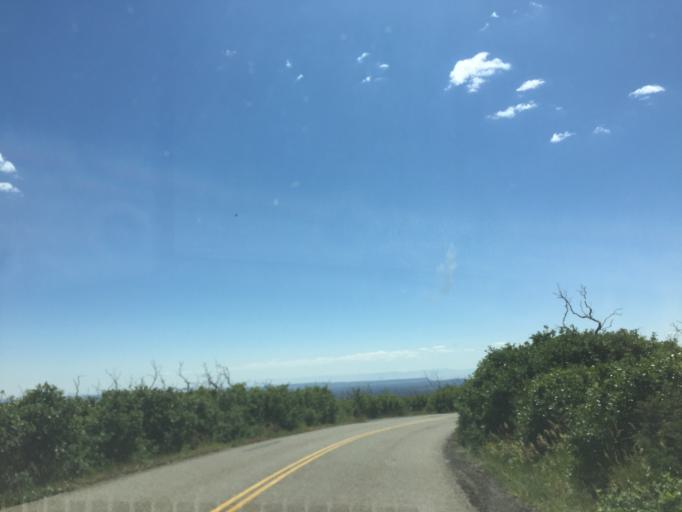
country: US
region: Colorado
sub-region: Montezuma County
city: Cortez
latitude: 37.2759
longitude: -108.4611
